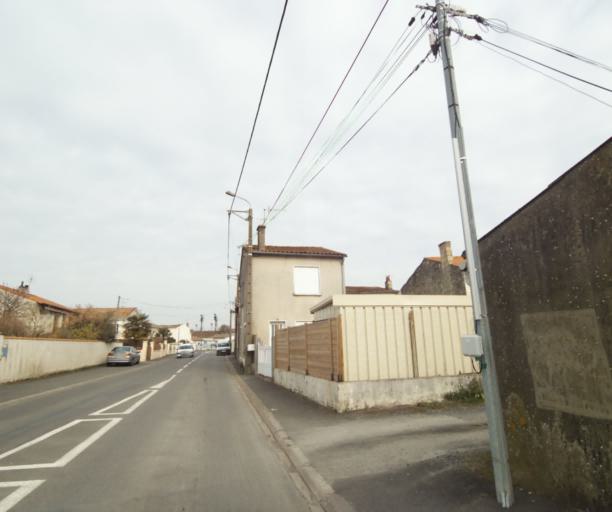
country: FR
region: Poitou-Charentes
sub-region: Departement des Deux-Sevres
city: Niort
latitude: 46.3092
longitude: -0.4610
